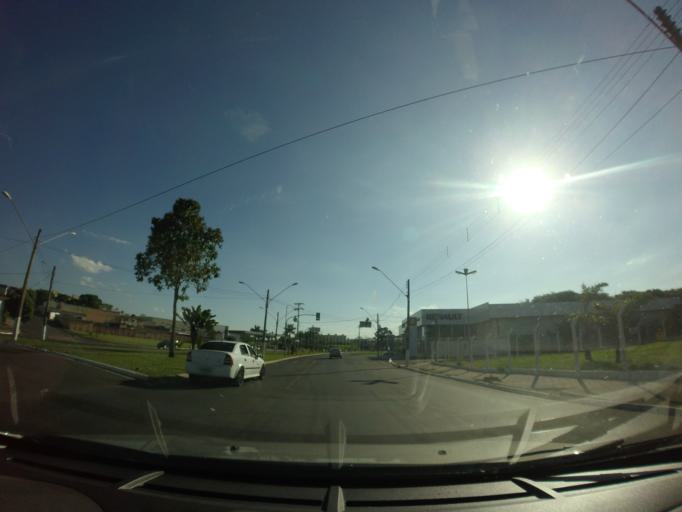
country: BR
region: Sao Paulo
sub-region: Rio Claro
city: Rio Claro
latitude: -22.4176
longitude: -47.5754
